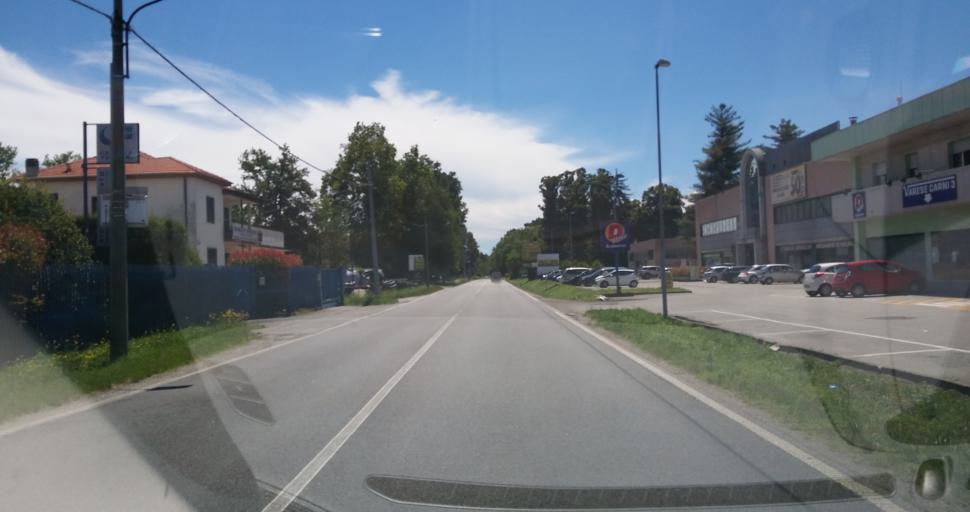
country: IT
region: Lombardy
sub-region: Provincia di Varese
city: Vergiate
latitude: 45.7139
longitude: 8.6934
